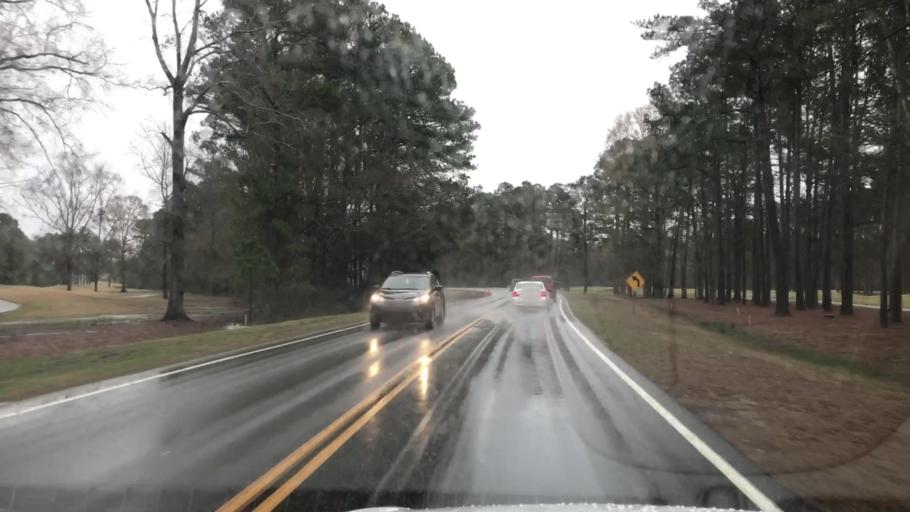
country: US
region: South Carolina
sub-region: Horry County
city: Forestbrook
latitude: 33.7280
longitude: -78.9133
